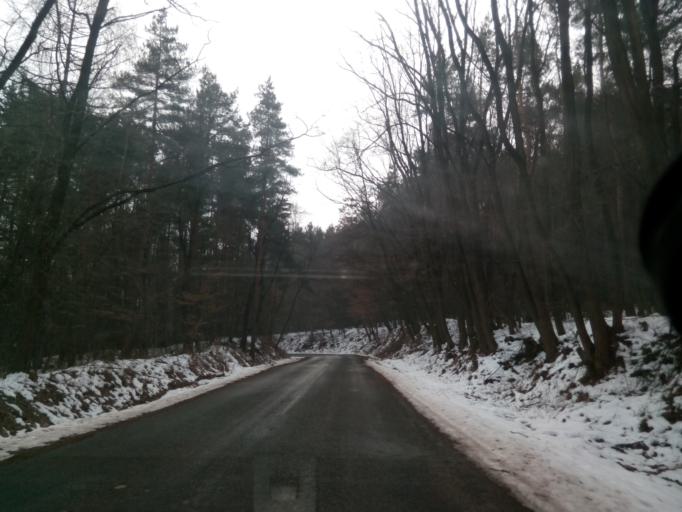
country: HU
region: Borsod-Abauj-Zemplen
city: Gonc
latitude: 48.4825
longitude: 21.3904
